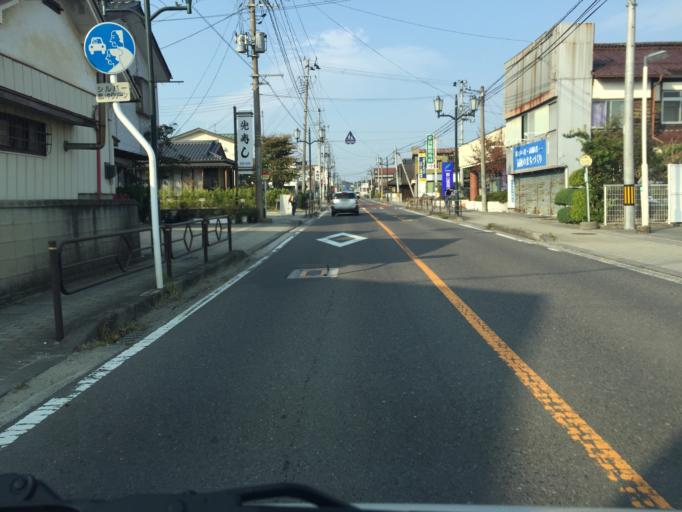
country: JP
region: Fukushima
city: Koriyama
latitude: 37.4212
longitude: 140.3914
